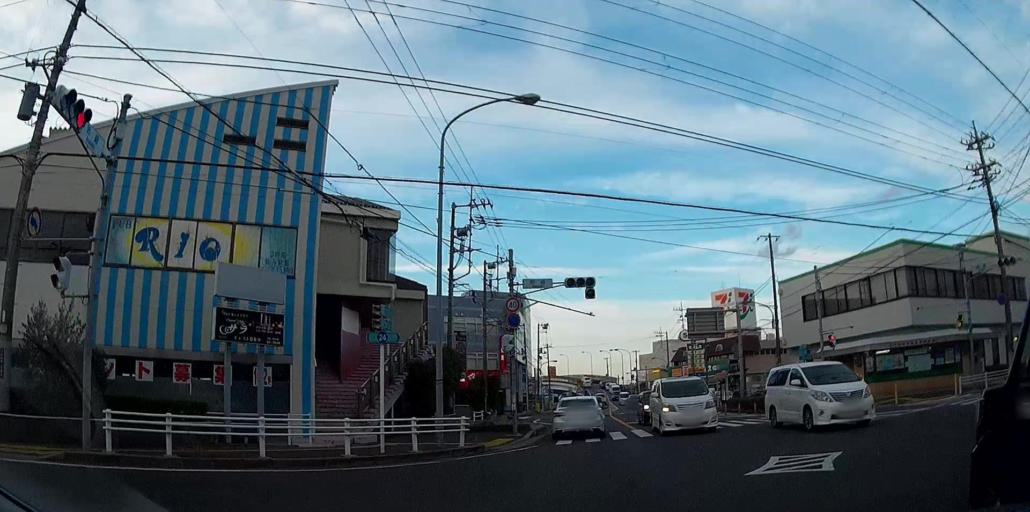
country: JP
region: Chiba
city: Ichihara
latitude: 35.4782
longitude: 140.0447
